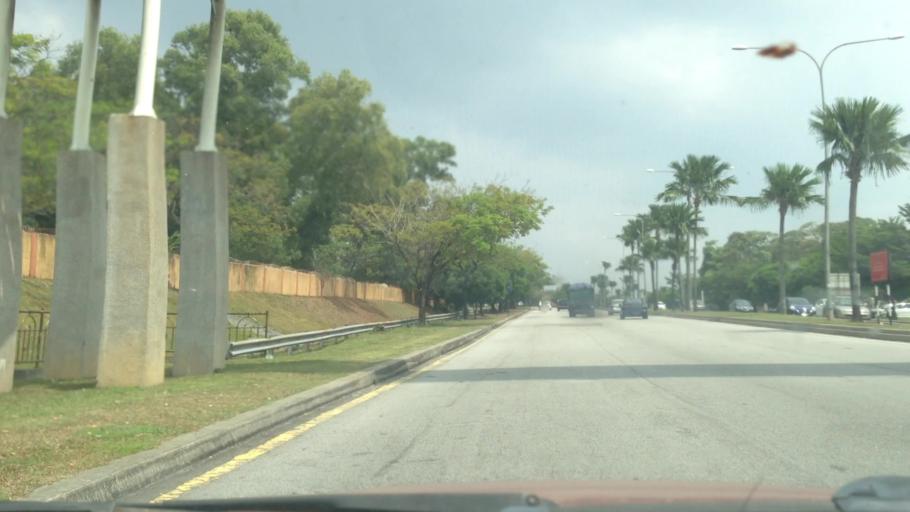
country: MY
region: Selangor
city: Subang Jaya
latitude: 3.0393
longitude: 101.5815
